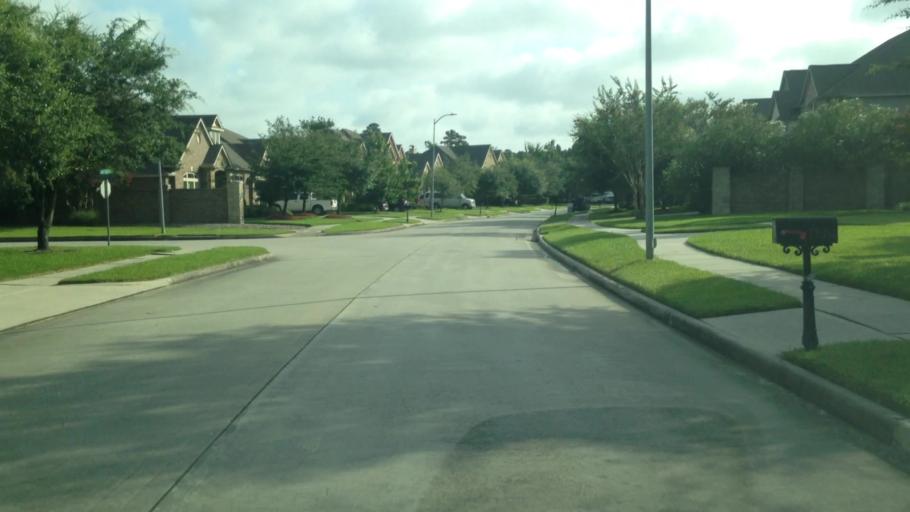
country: US
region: Texas
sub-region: Harris County
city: Sheldon
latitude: 29.9222
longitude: -95.1708
